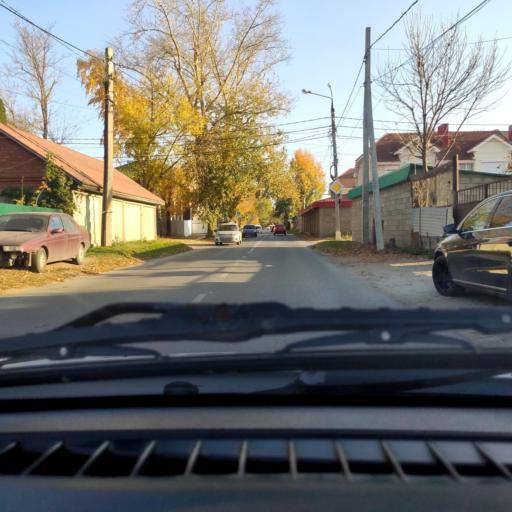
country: RU
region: Samara
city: Tol'yatti
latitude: 53.5137
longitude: 49.4004
